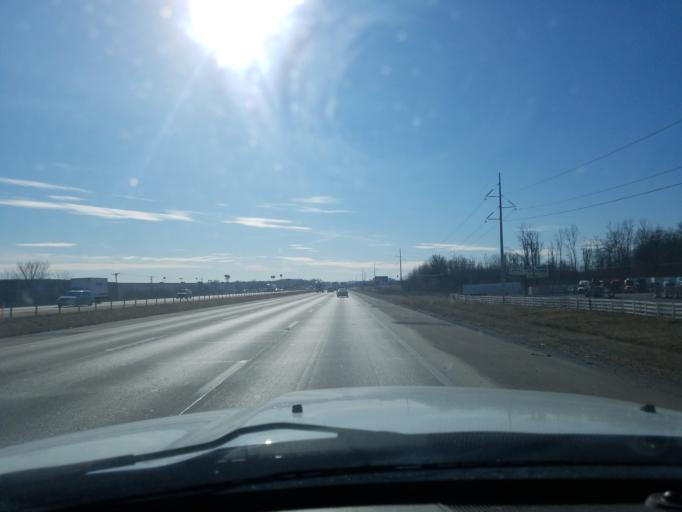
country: US
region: Kentucky
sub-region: Bullitt County
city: Hillview
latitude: 38.0744
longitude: -85.7003
